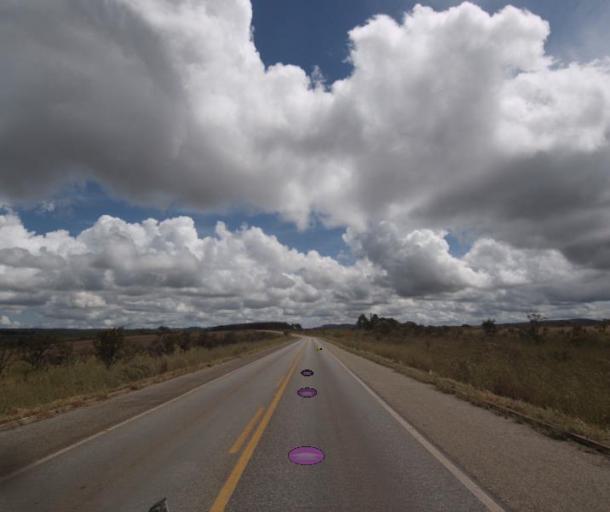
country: BR
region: Goias
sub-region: Pirenopolis
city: Pirenopolis
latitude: -15.7487
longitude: -48.6629
